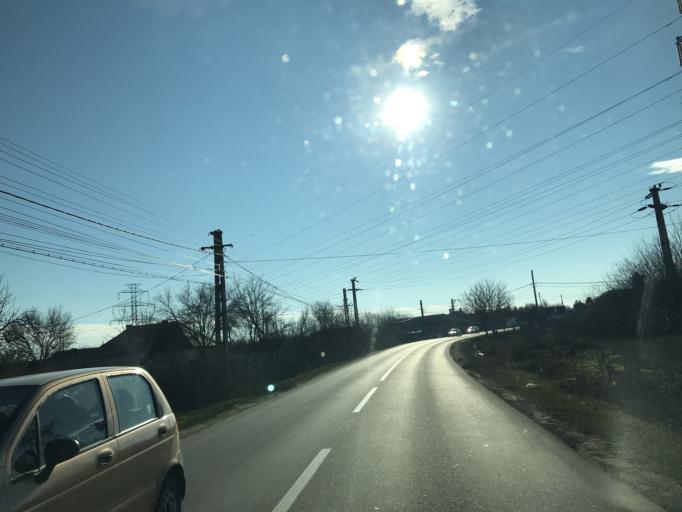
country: RO
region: Olt
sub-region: Comuna Slatioara
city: Slatioara
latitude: 44.4120
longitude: 24.3261
